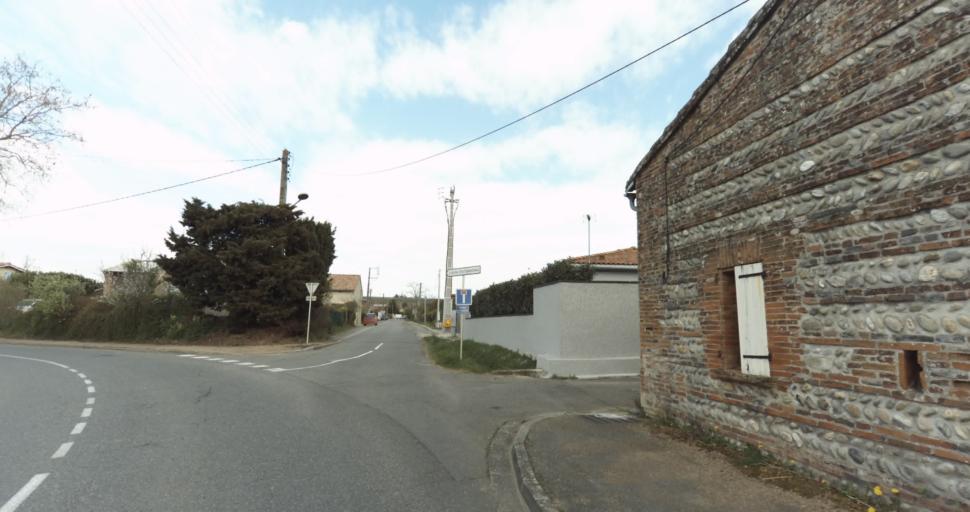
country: FR
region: Midi-Pyrenees
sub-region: Departement de la Haute-Garonne
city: Auterive
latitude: 43.3554
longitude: 1.4784
